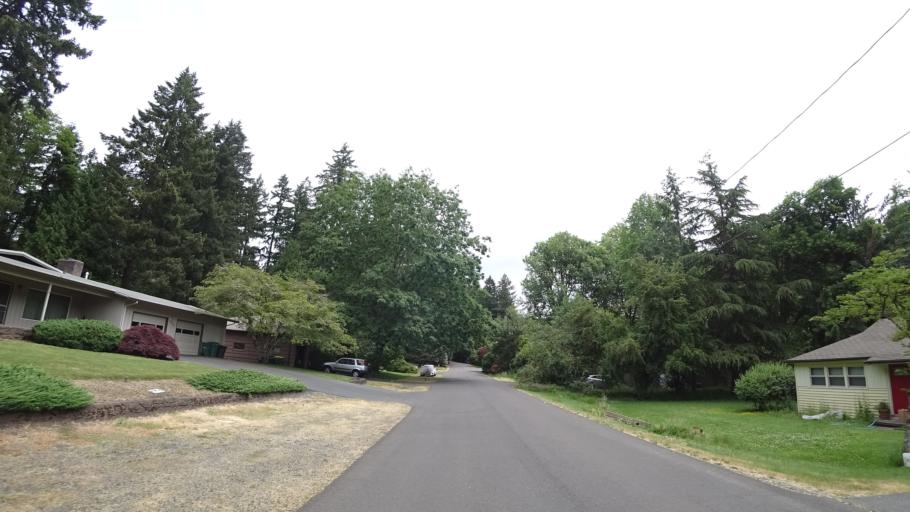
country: US
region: Oregon
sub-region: Washington County
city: Garden Home-Whitford
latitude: 45.4590
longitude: -122.7563
